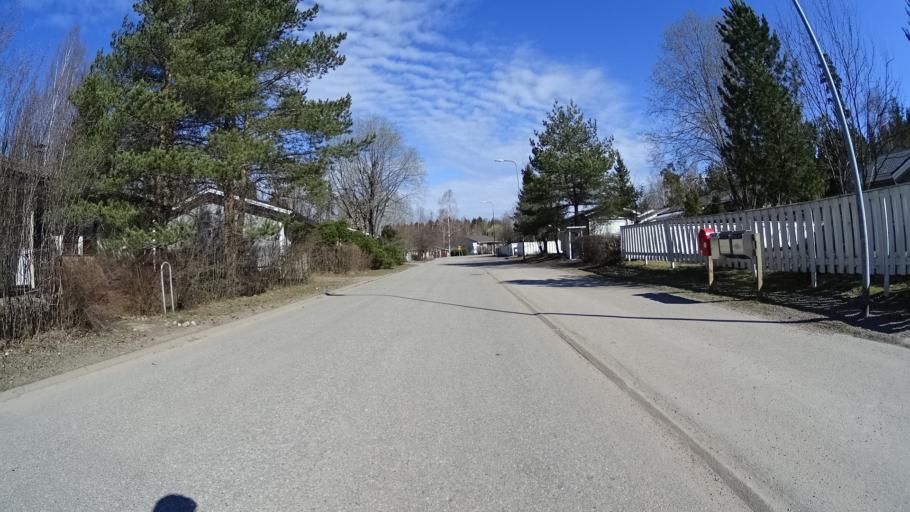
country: FI
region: Uusimaa
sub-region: Helsinki
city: Kilo
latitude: 60.2794
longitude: 24.7527
